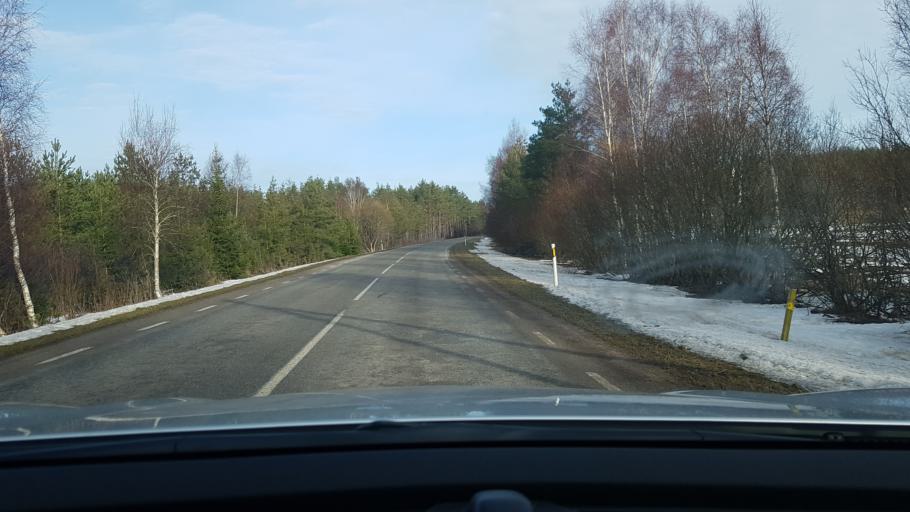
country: EE
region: Saare
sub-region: Kuressaare linn
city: Kuressaare
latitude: 58.4786
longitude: 22.7037
